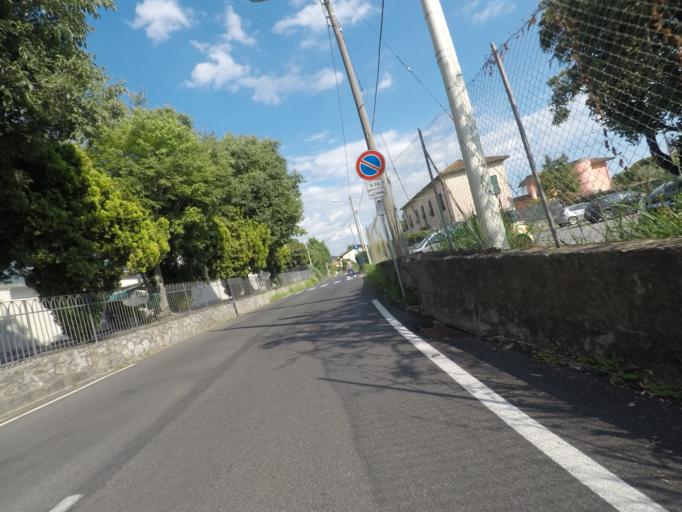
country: IT
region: Tuscany
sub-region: Provincia di Massa-Carrara
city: Massa
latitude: 44.0219
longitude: 10.1407
